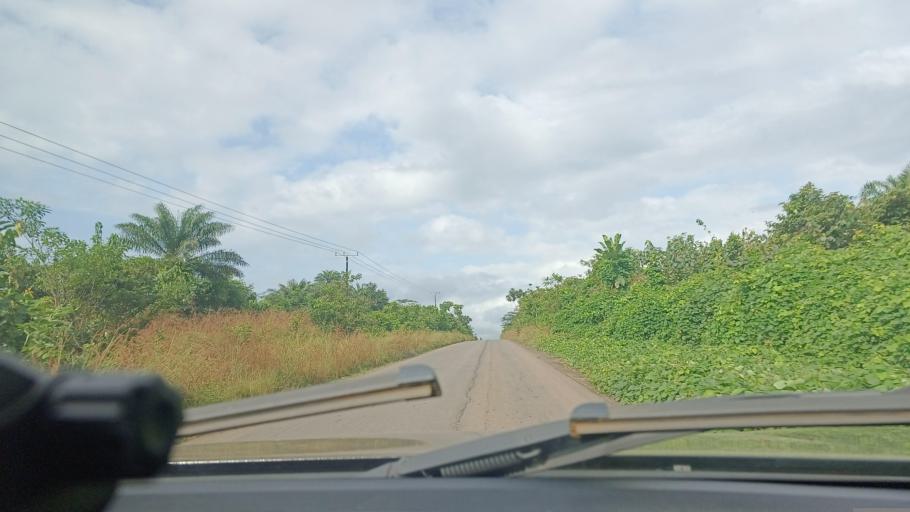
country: LR
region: Bomi
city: Tubmanburg
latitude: 6.7313
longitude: -11.0028
